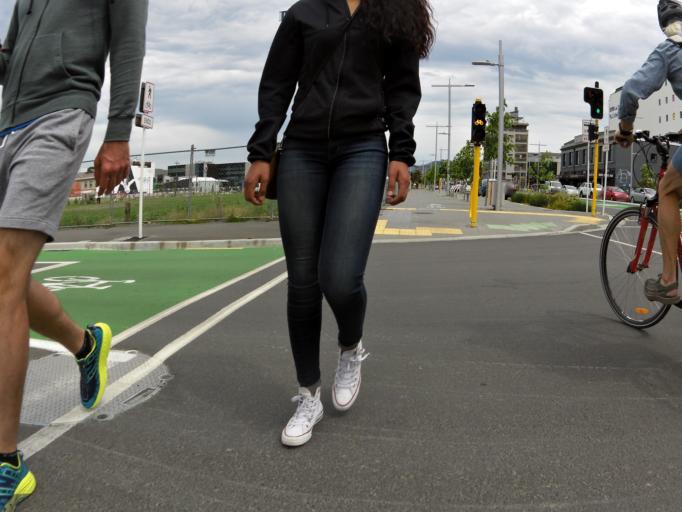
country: NZ
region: Canterbury
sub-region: Christchurch City
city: Christchurch
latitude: -43.5322
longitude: 172.6397
